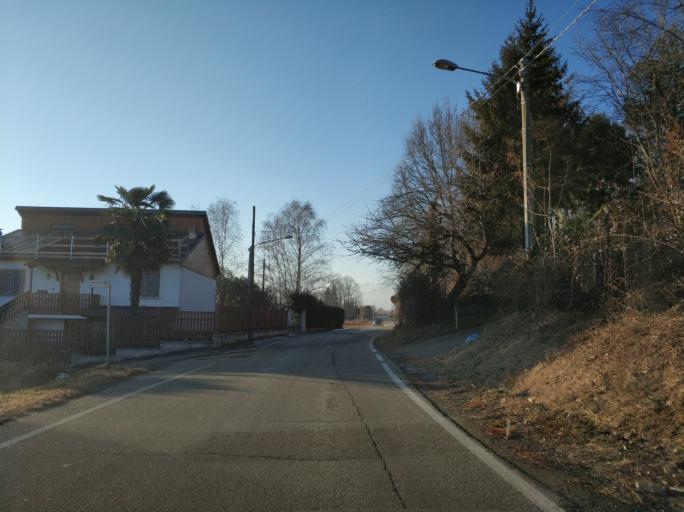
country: IT
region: Piedmont
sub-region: Provincia di Torino
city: San Francesco al Campo
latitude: 45.2287
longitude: 7.6424
